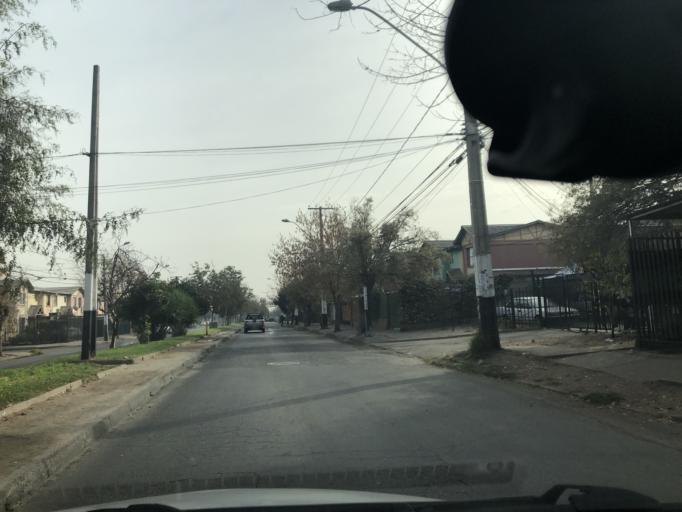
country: CL
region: Santiago Metropolitan
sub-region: Provincia de Cordillera
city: Puente Alto
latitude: -33.5858
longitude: -70.5553
